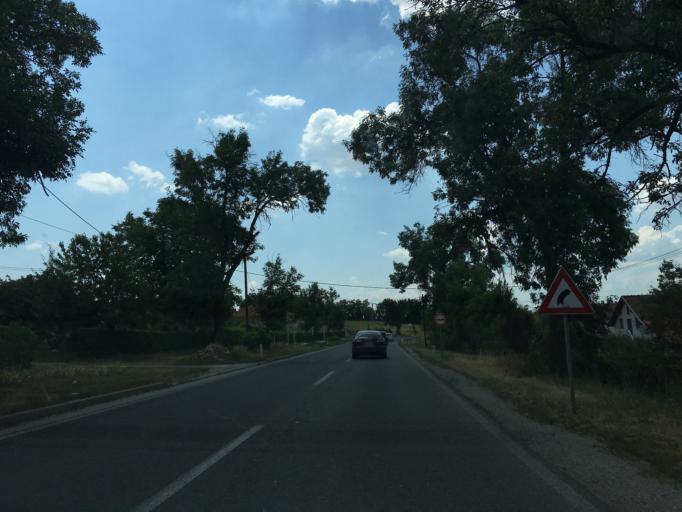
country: RS
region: Central Serbia
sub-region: Belgrade
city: Mladenovac
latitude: 44.4651
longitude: 20.6680
